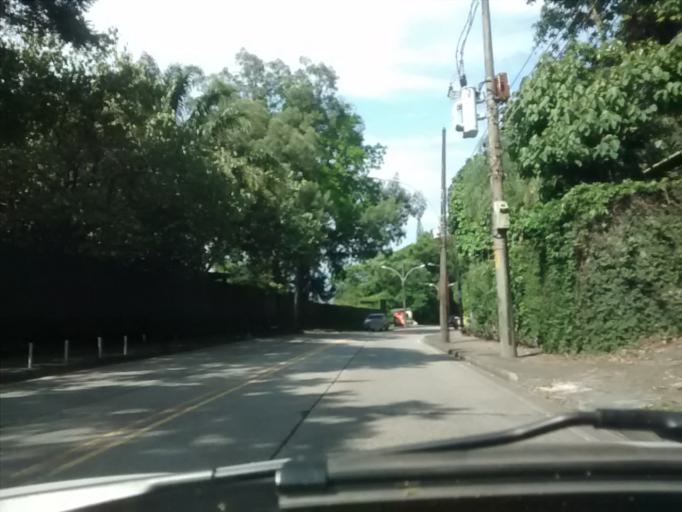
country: BR
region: Rio de Janeiro
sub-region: Rio De Janeiro
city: Rio de Janeiro
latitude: -22.9541
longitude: -43.2625
